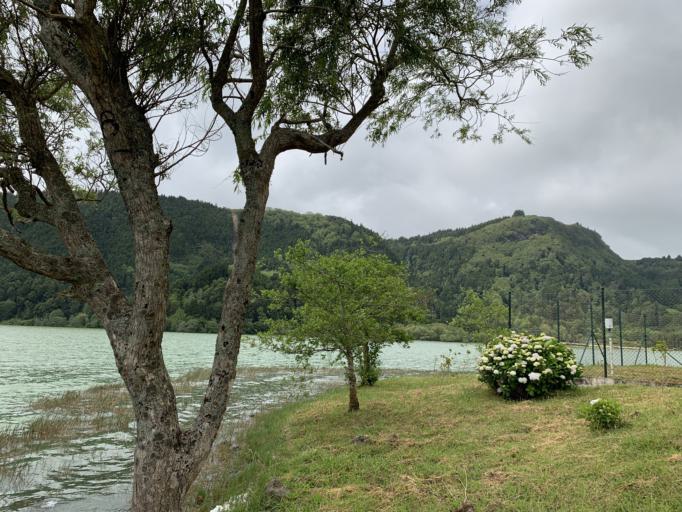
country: PT
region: Azores
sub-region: Povoacao
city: Furnas
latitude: 37.7618
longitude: -25.3291
